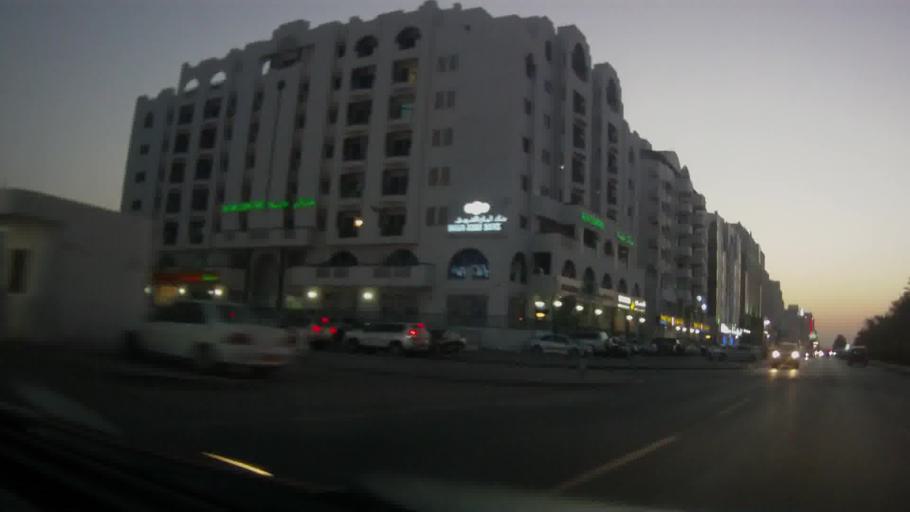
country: OM
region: Muhafazat Masqat
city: Bawshar
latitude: 23.5968
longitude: 58.4317
